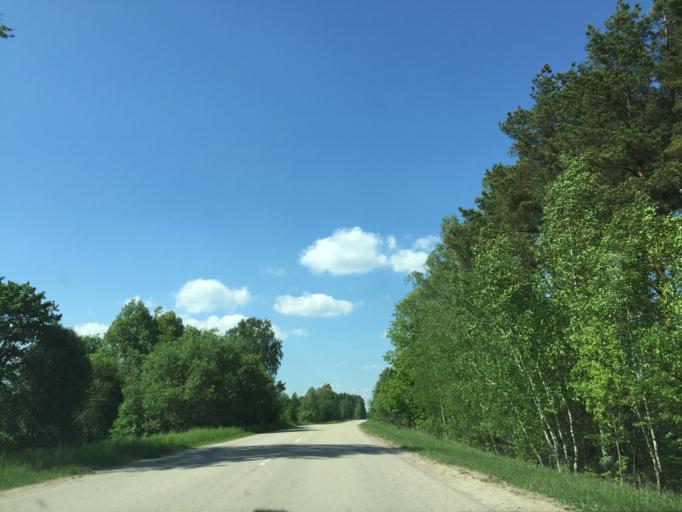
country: LV
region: Ozolnieku
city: Ozolnieki
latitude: 56.6036
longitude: 23.9481
